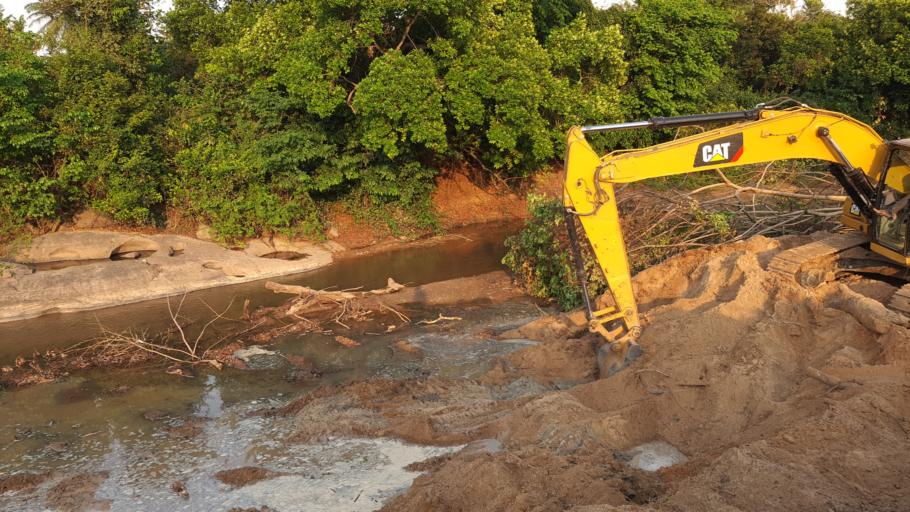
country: NG
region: Osun
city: Iwo
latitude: 7.7369
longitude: 4.0847
